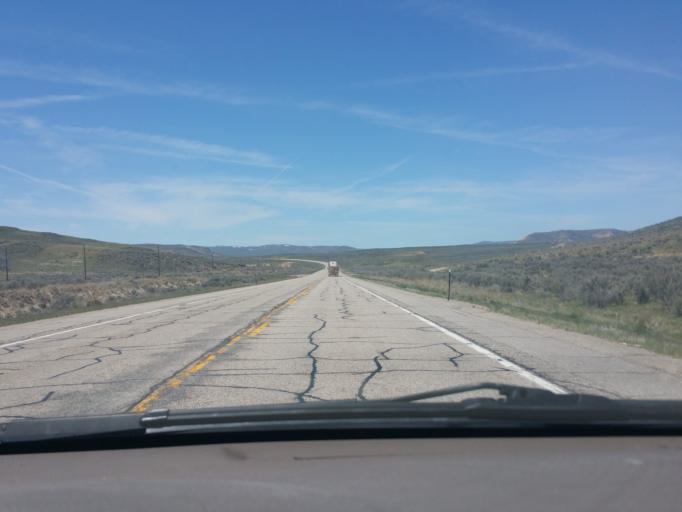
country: US
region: Wyoming
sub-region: Lincoln County
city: Kemmerer
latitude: 41.8159
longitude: -110.6489
